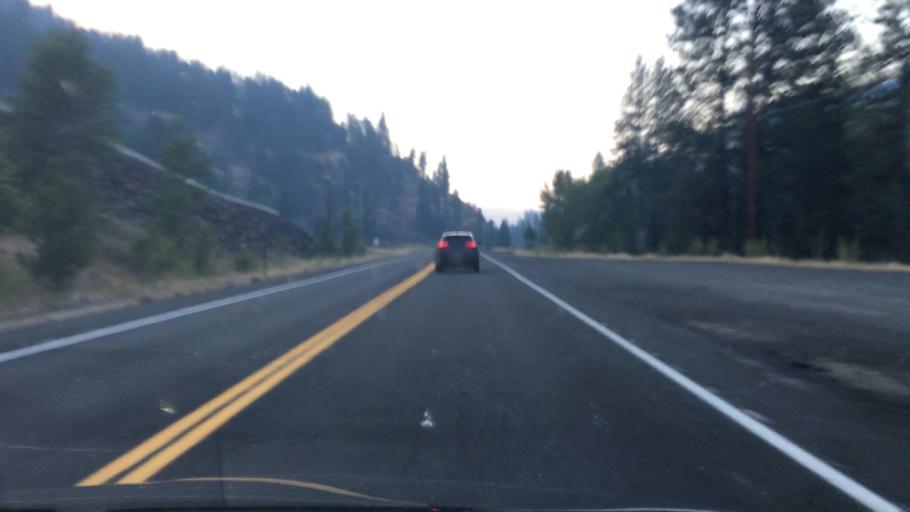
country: US
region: Idaho
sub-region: Valley County
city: McCall
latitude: 45.2158
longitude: -116.3166
